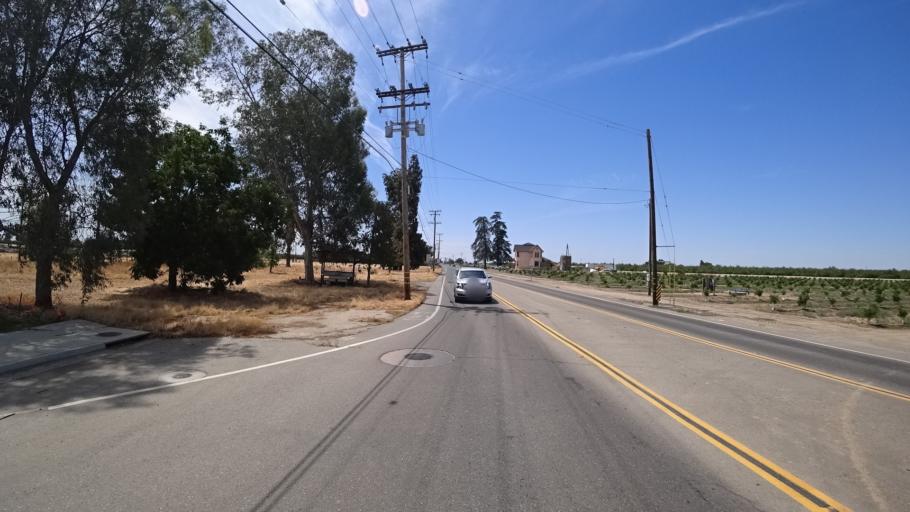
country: US
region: California
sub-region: Kings County
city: Armona
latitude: 36.3317
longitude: -119.6910
